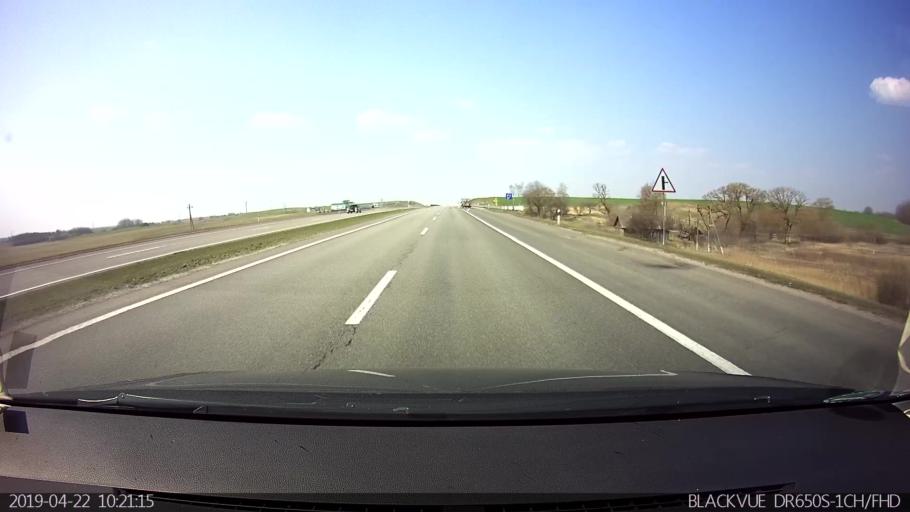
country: BY
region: Vitebsk
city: Kokhanava
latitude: 54.5054
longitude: 30.1090
